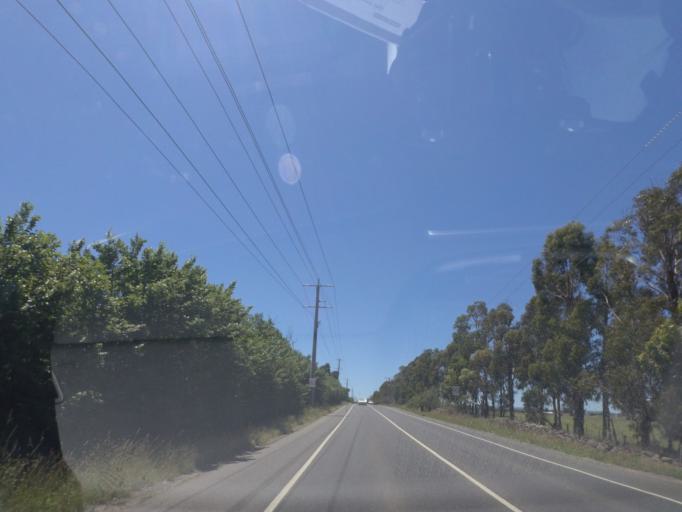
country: AU
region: Victoria
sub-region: Whittlesea
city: Epping
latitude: -37.6050
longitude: 145.0319
